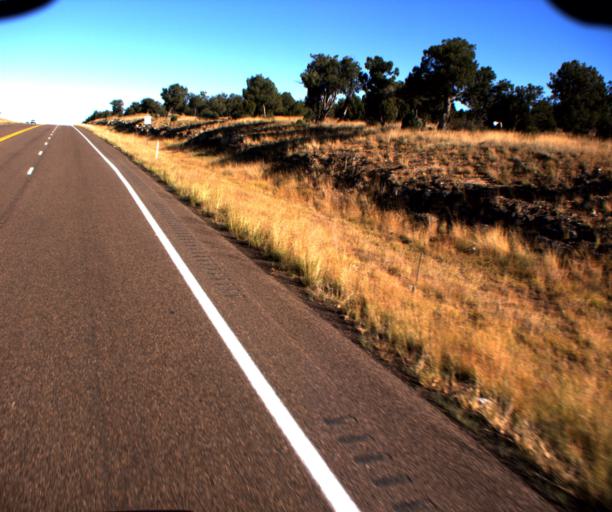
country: US
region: Arizona
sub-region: Navajo County
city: White Mountain Lake
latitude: 34.3314
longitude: -110.0471
